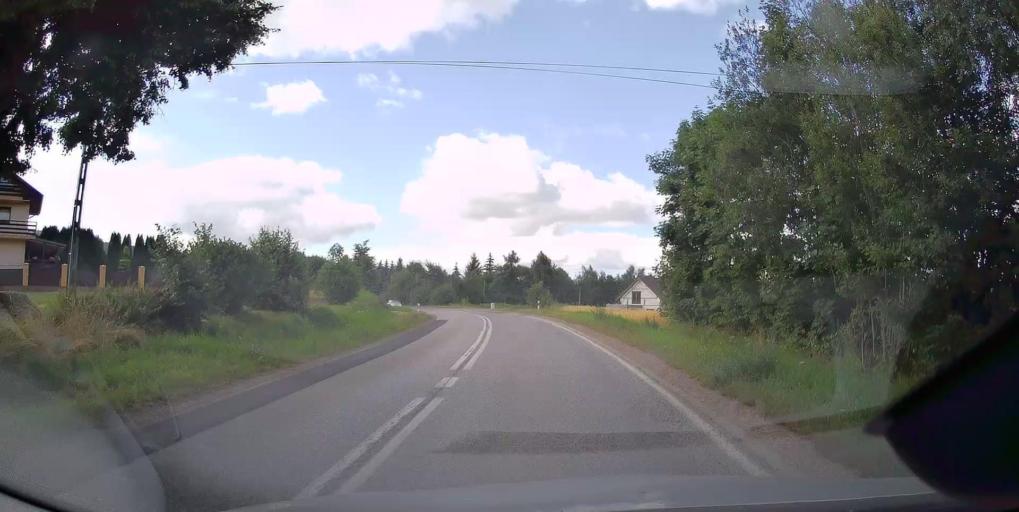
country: PL
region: Swietokrzyskie
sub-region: Powiat kielecki
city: Nowa Slupia
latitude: 50.8464
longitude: 21.0885
